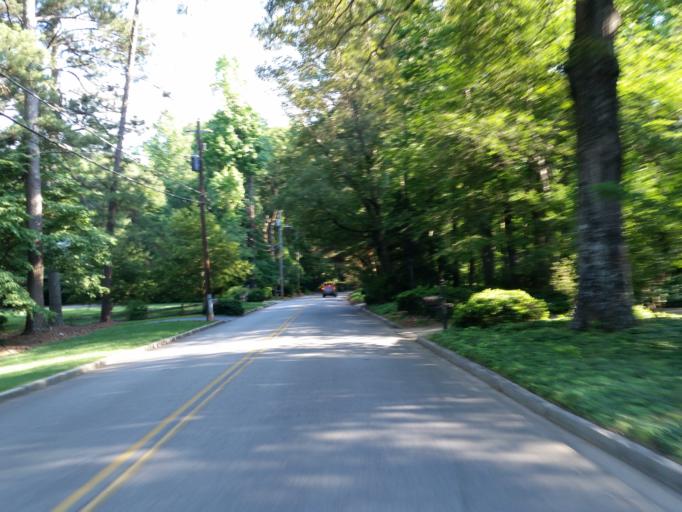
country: US
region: Georgia
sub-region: Cobb County
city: Vinings
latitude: 33.8550
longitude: -84.4220
